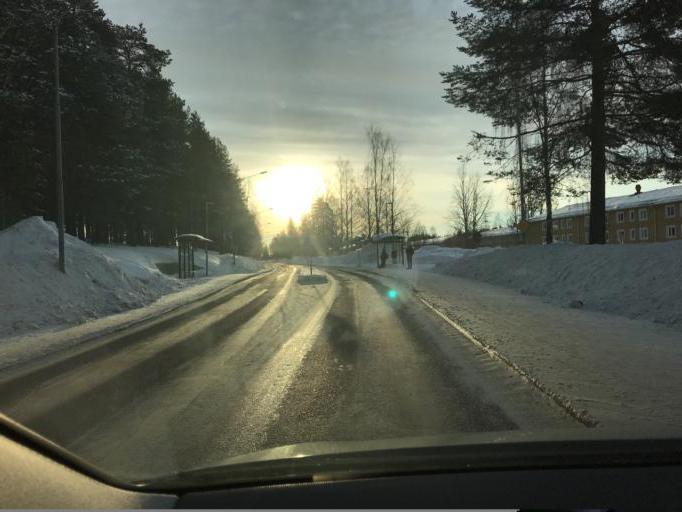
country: SE
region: Norrbotten
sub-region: Lulea Kommun
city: Bergnaset
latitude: 65.6093
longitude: 22.1019
